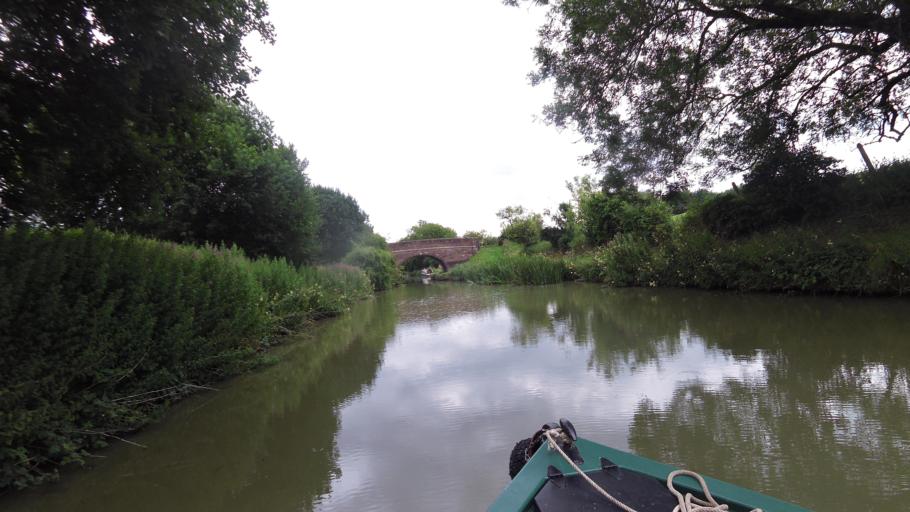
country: GB
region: England
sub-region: Wiltshire
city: Burbage
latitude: 51.3612
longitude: -1.6504
